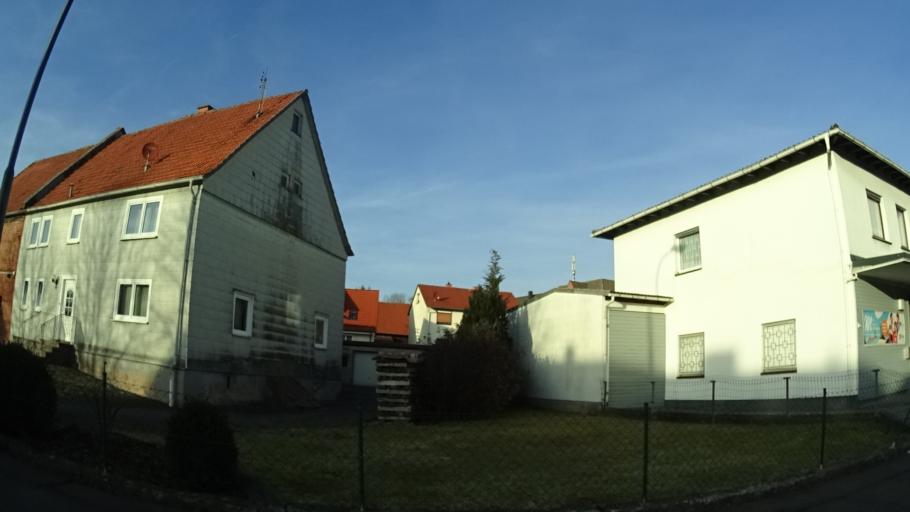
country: DE
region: Bavaria
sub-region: Regierungsbezirk Unterfranken
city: Zeitlofs
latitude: 50.3127
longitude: 9.6220
